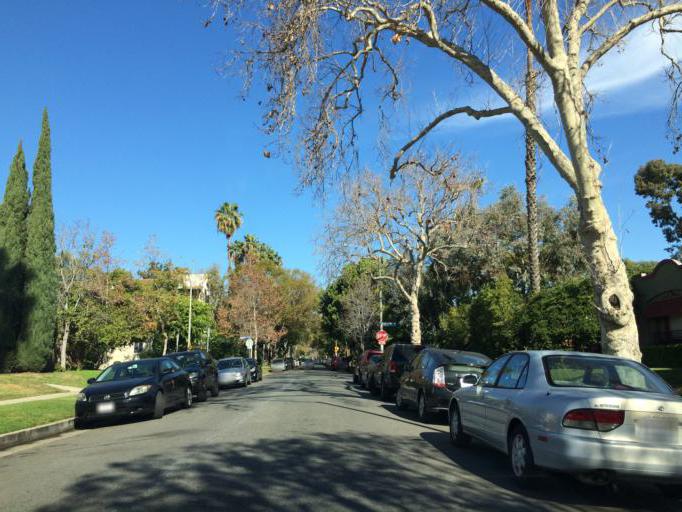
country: US
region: California
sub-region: Los Angeles County
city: West Hollywood
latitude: 34.0866
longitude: -118.3511
